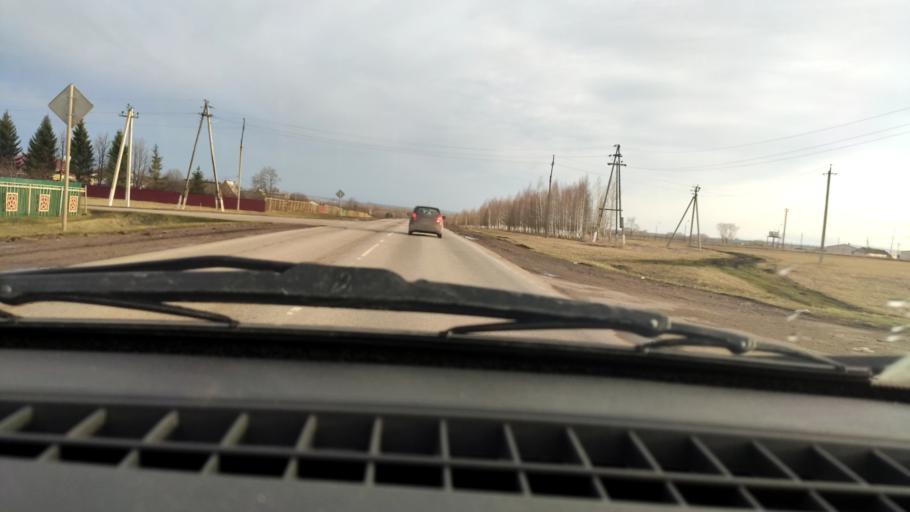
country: RU
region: Bashkortostan
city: Davlekanovo
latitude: 54.3781
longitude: 55.1956
